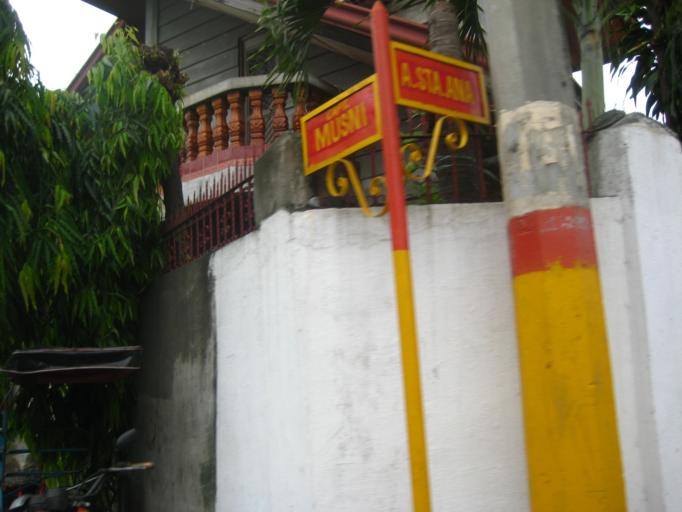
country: PH
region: Calabarzon
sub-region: Province of Rizal
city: Pateros
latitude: 14.5467
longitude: 121.0764
